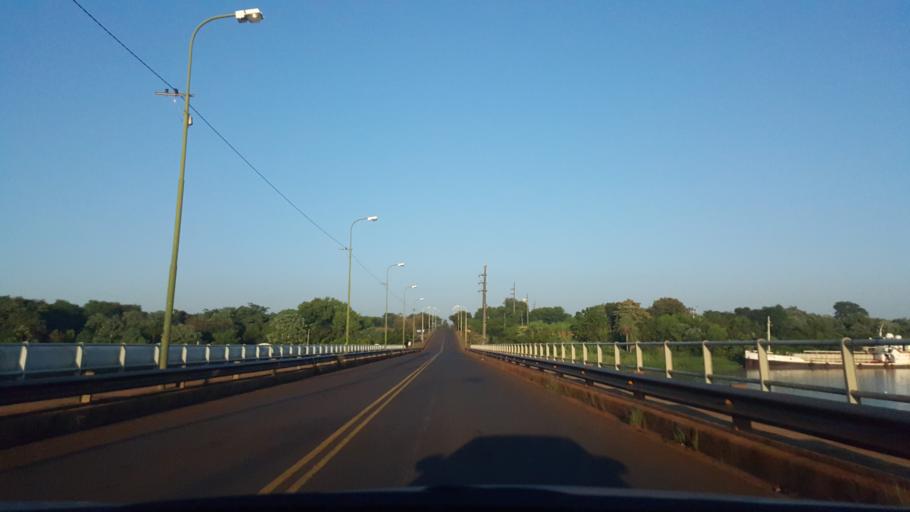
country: AR
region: Misiones
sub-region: Departamento de Capital
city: Posadas
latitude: -27.3723
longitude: -55.9564
